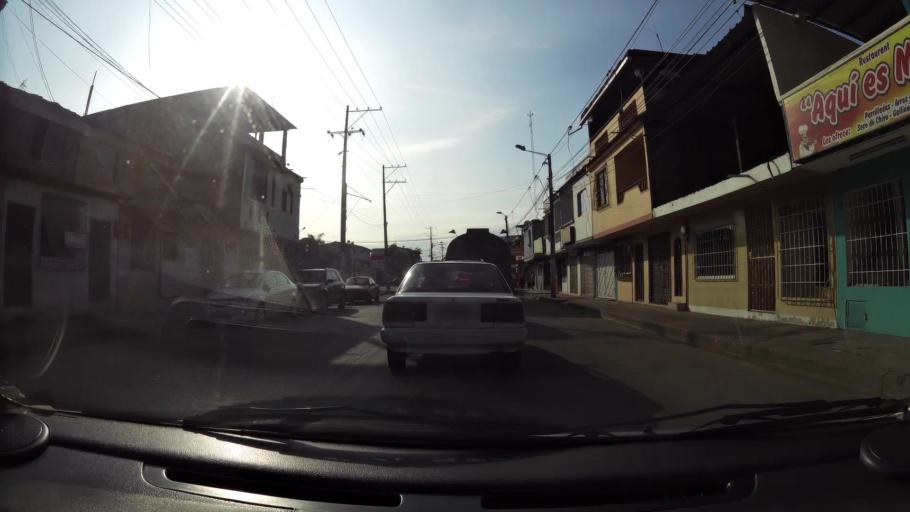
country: EC
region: Guayas
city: Eloy Alfaro
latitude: -2.1798
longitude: -79.8544
